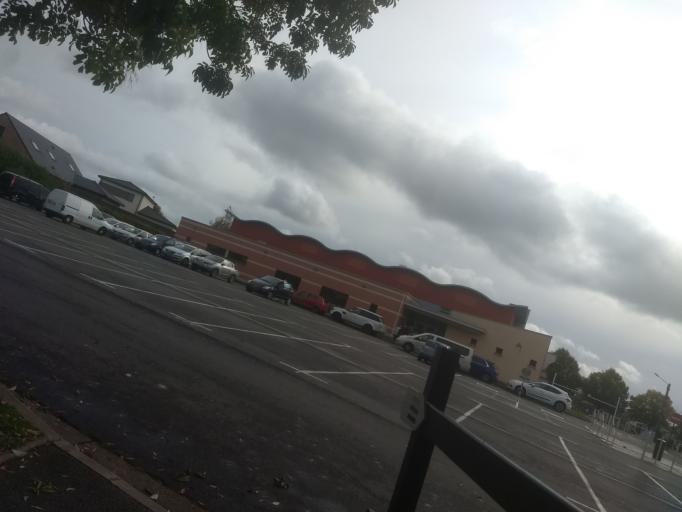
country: FR
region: Nord-Pas-de-Calais
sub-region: Departement du Pas-de-Calais
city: Anzin-Saint-Aubin
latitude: 50.3123
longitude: 2.7505
